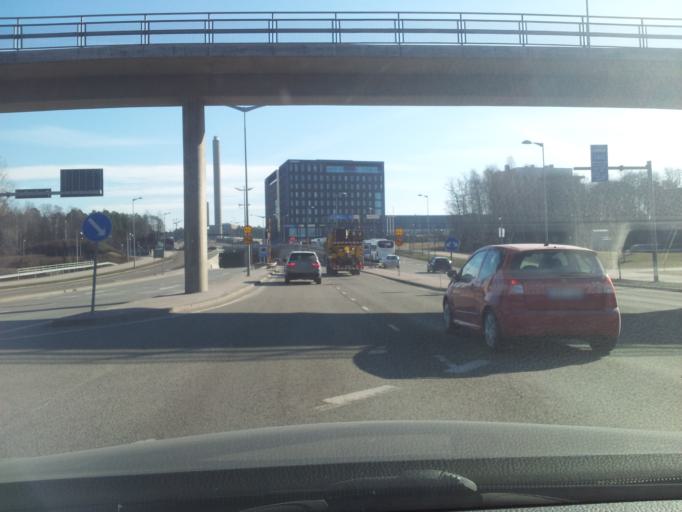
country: FI
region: Uusimaa
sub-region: Helsinki
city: Helsinki
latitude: 60.2084
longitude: 24.8951
